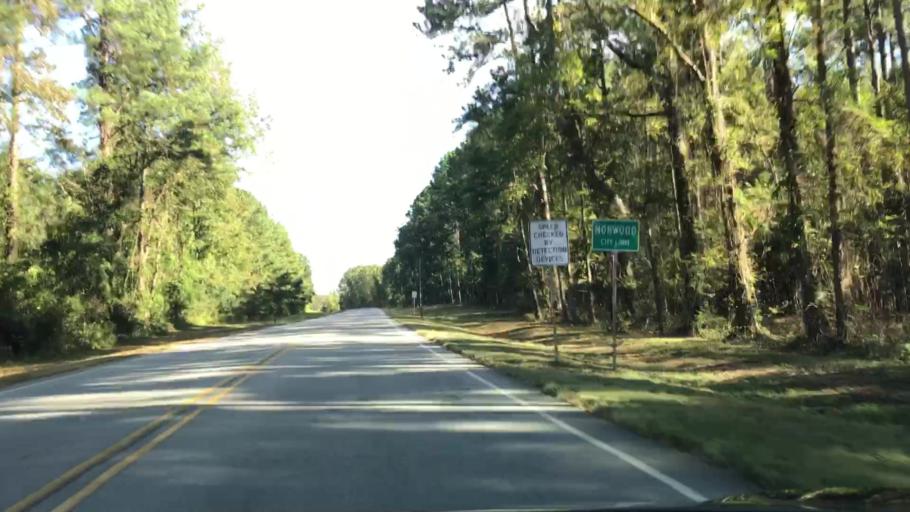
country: US
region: Georgia
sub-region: Warren County
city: Firing Range
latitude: 33.4660
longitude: -82.7128
